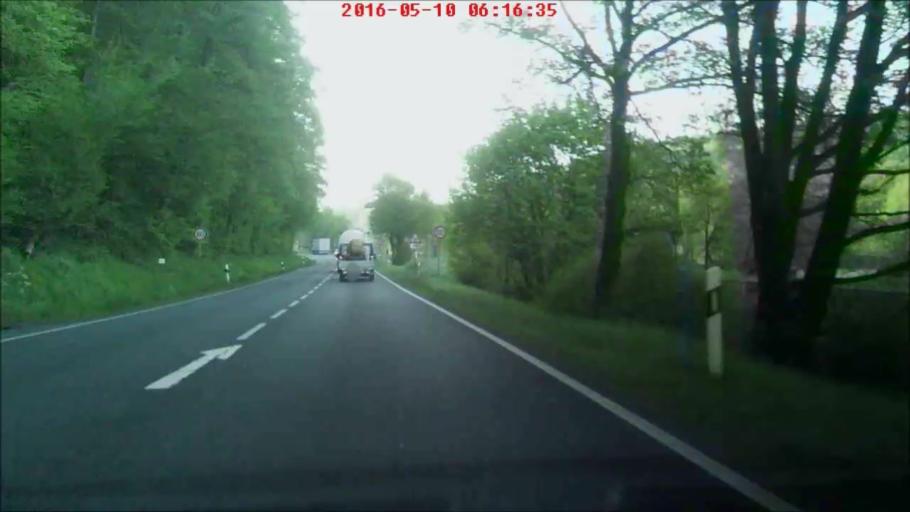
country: DE
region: Hesse
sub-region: Regierungsbezirk Kassel
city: Burghaun
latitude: 50.7420
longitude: 9.6893
